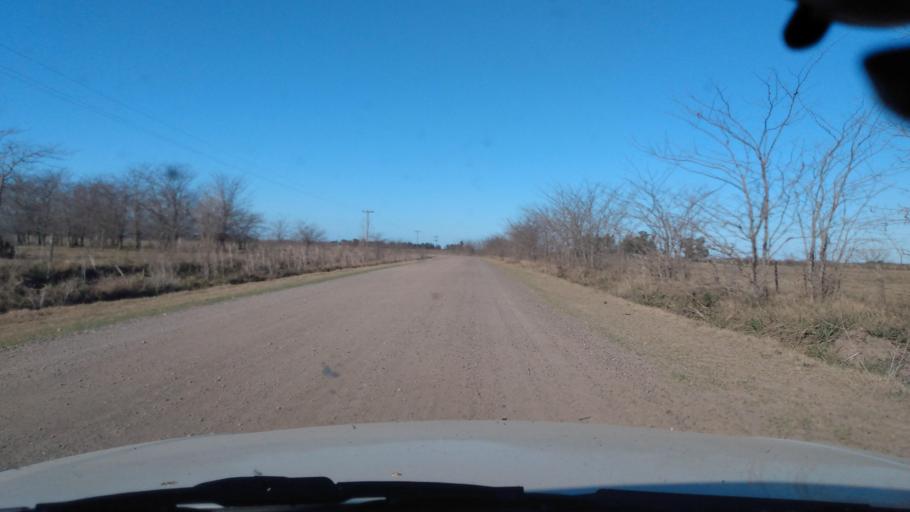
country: AR
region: Buenos Aires
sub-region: Partido de Mercedes
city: Mercedes
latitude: -34.6121
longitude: -59.3225
